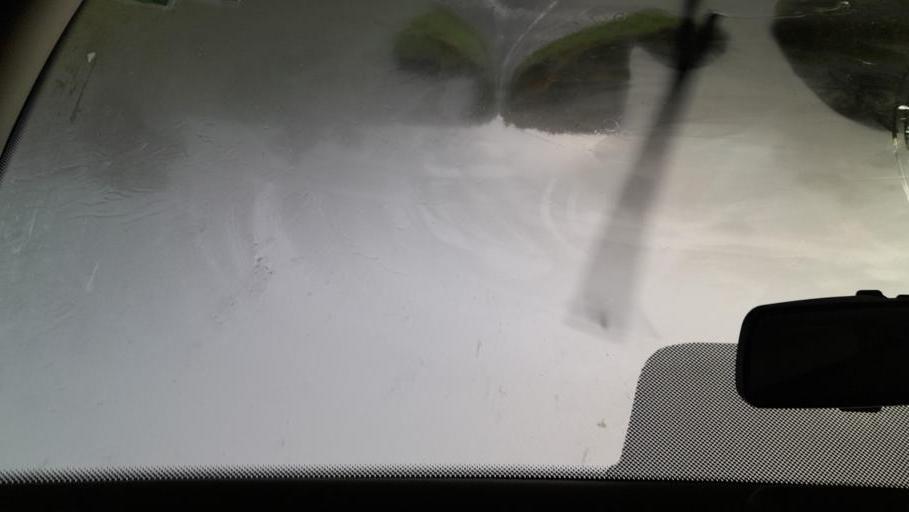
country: FR
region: Pays de la Loire
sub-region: Departement de la Mayenne
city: Ballots
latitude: 47.8723
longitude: -1.0470
